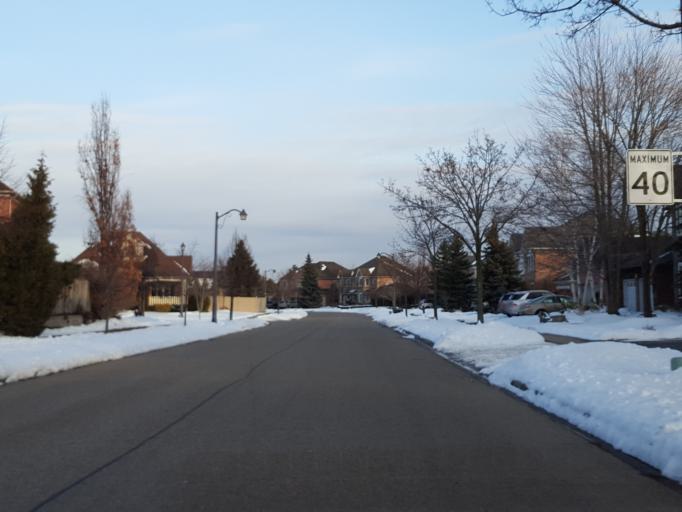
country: CA
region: Ontario
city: Burlington
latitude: 43.3933
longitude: -79.8037
